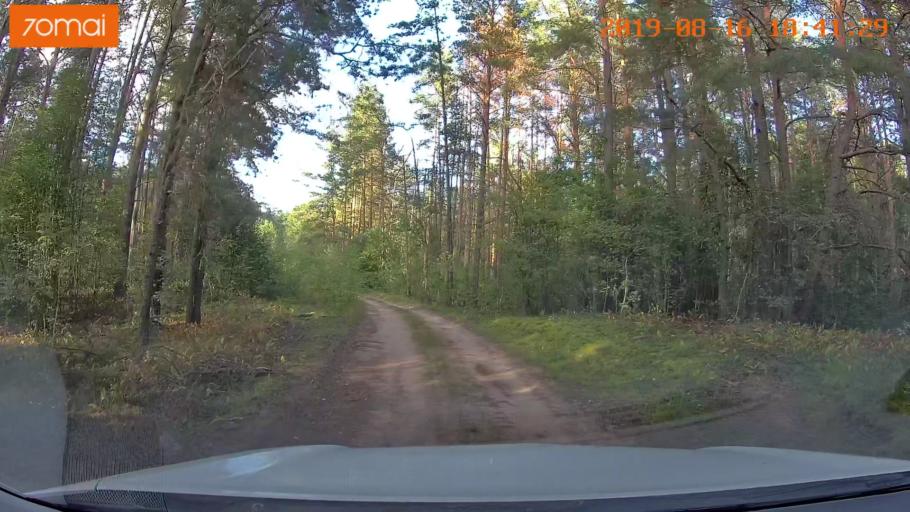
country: BY
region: Mogilev
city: Asipovichy
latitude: 53.2126
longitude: 28.6449
